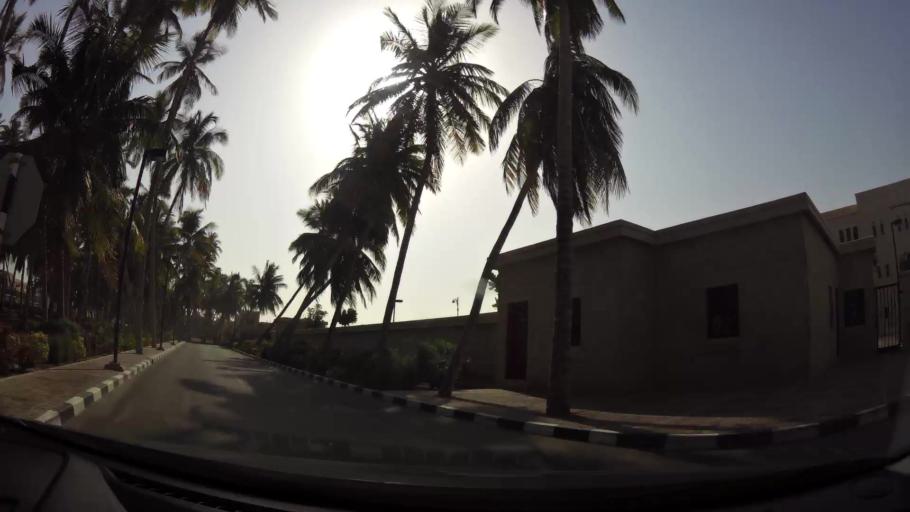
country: OM
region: Zufar
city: Salalah
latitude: 17.0007
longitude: 54.1002
